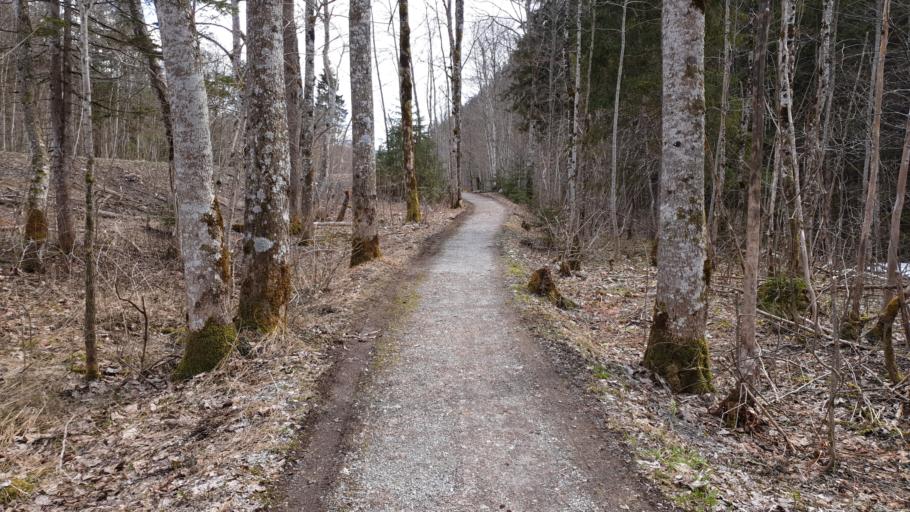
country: DE
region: Bavaria
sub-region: Upper Bavaria
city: Bayrischzell
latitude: 47.6460
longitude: 12.0084
